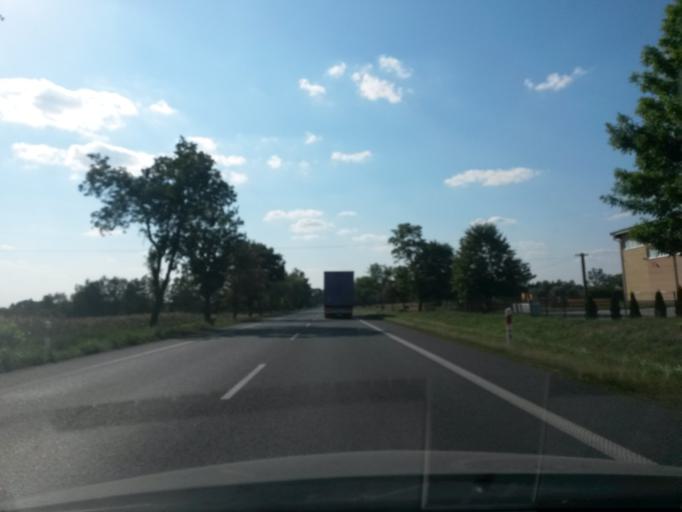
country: PL
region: Masovian Voivodeship
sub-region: Powiat sierpecki
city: Zawidz
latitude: 52.8085
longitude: 19.8312
